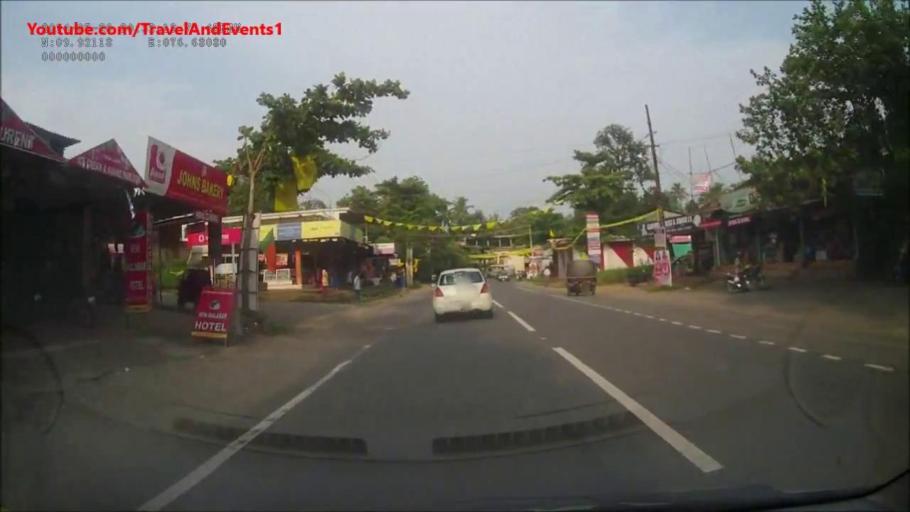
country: IN
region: Kerala
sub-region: Ernakulam
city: Muvattupula
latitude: 9.9214
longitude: 76.6802
